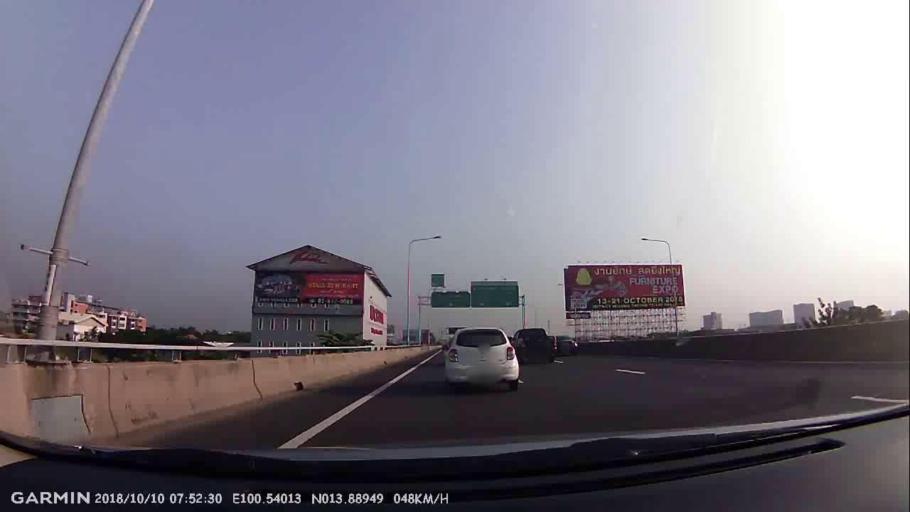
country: TH
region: Nonthaburi
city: Mueang Nonthaburi
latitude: 13.8896
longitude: 100.5402
